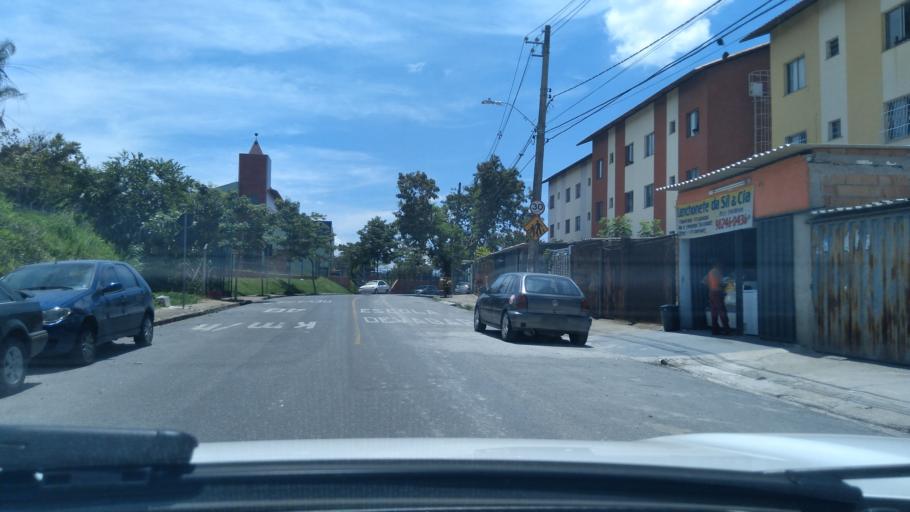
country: BR
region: Minas Gerais
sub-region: Contagem
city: Contagem
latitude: -19.9271
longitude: -44.0164
